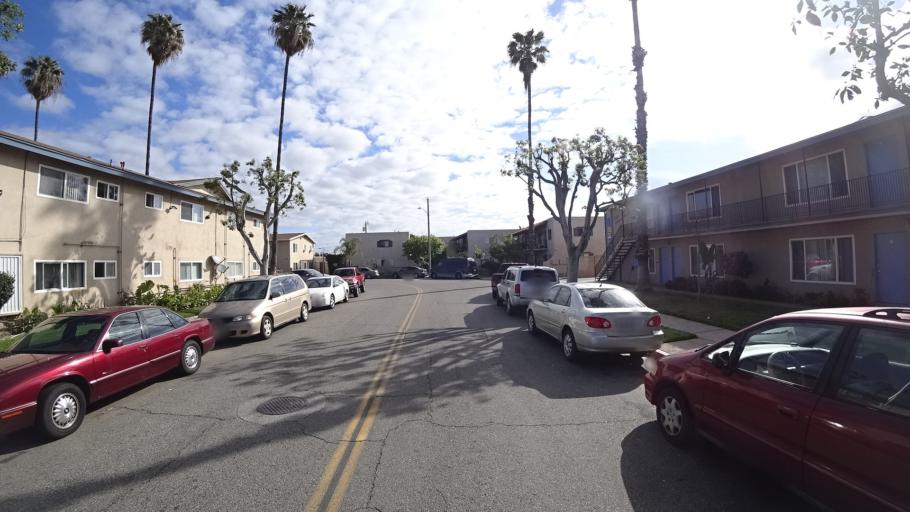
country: US
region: California
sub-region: Orange County
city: Anaheim
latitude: 33.8454
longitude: -117.8967
